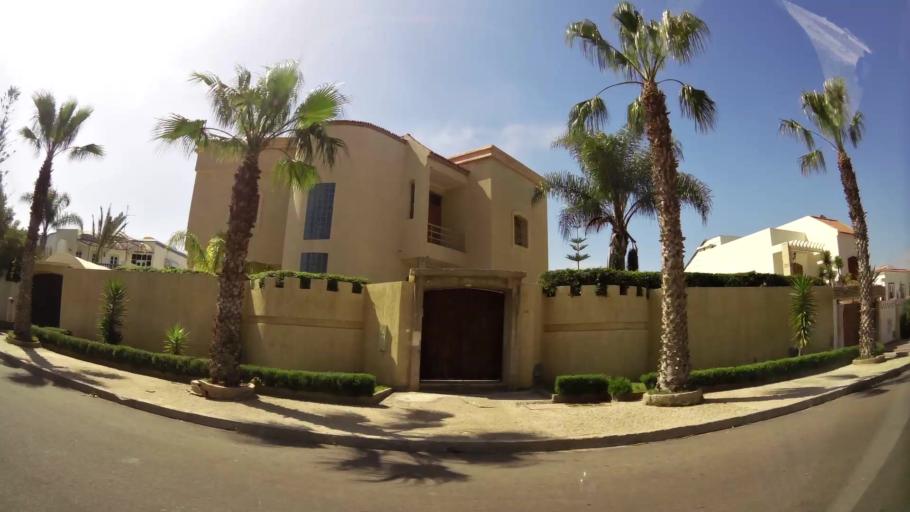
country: MA
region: Souss-Massa-Draa
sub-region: Agadir-Ida-ou-Tnan
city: Agadir
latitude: 30.4409
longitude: -9.5930
